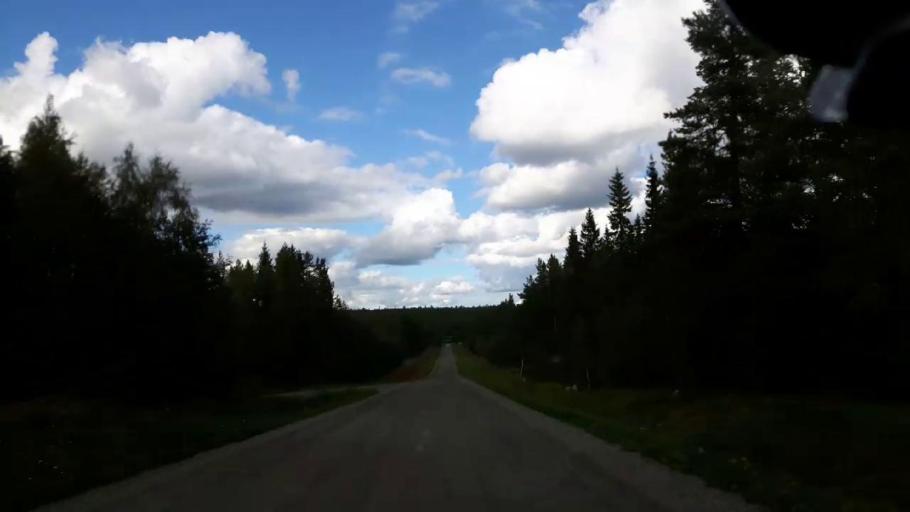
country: SE
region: Jaemtland
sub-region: Stroemsunds Kommun
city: Stroemsund
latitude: 63.4096
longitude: 15.5627
